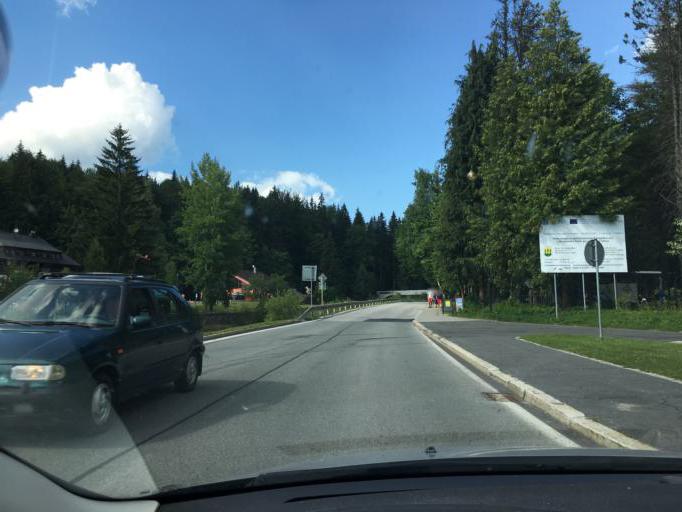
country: CZ
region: Kralovehradecky
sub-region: Okres Trutnov
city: Spindleruv Mlyn
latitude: 50.7261
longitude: 15.6066
